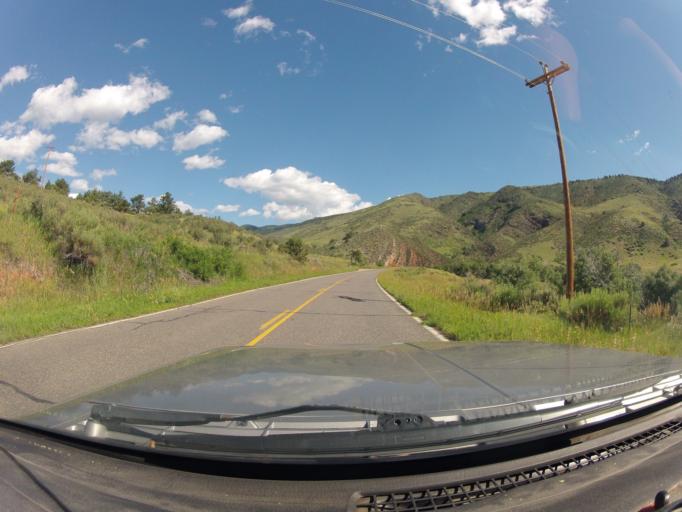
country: US
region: Colorado
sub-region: Larimer County
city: Laporte
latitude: 40.5063
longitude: -105.2292
